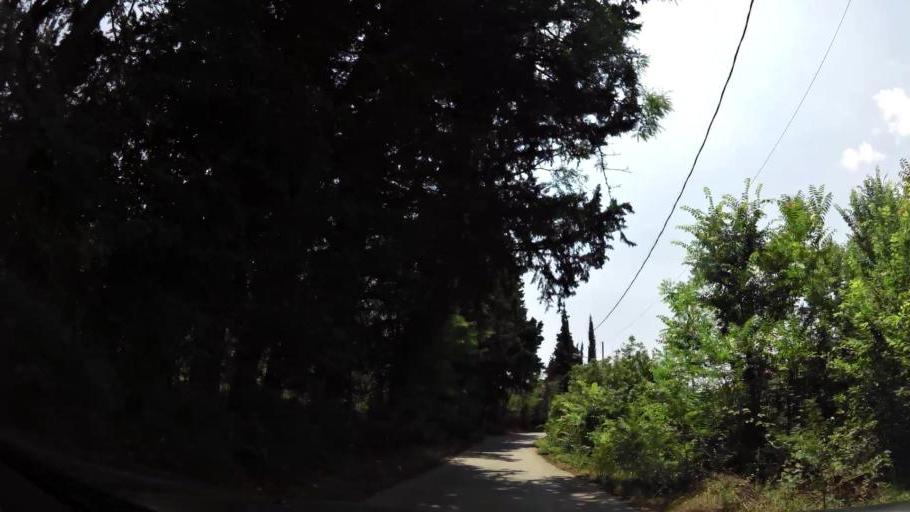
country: GR
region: Central Macedonia
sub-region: Nomos Imathias
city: Veroia
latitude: 40.5129
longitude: 22.1992
